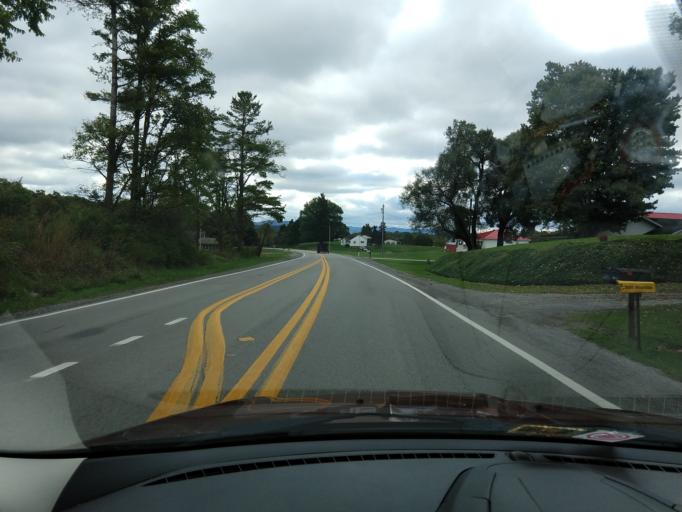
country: US
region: West Virginia
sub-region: Barbour County
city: Belington
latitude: 39.0612
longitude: -79.9703
